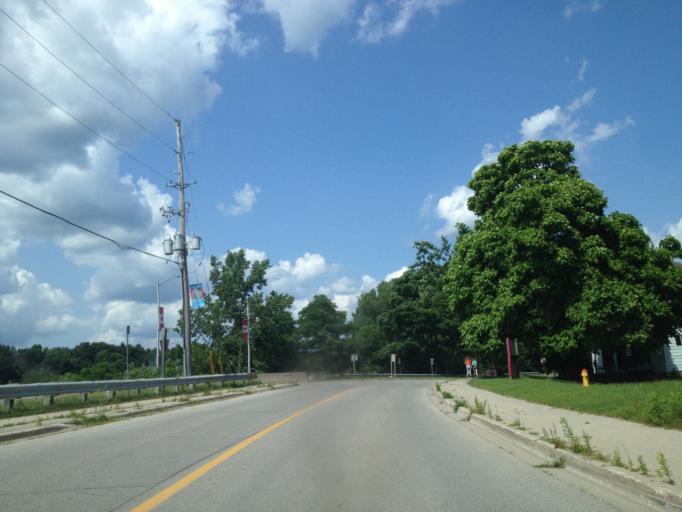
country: CA
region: Ontario
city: Aylmer
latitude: 42.6480
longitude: -80.8066
